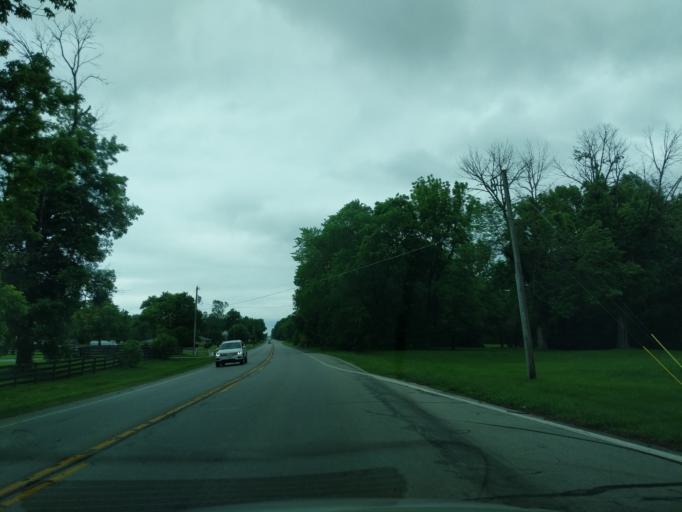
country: US
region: Indiana
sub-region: Hamilton County
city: Noblesville
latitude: 40.0690
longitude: -86.0148
